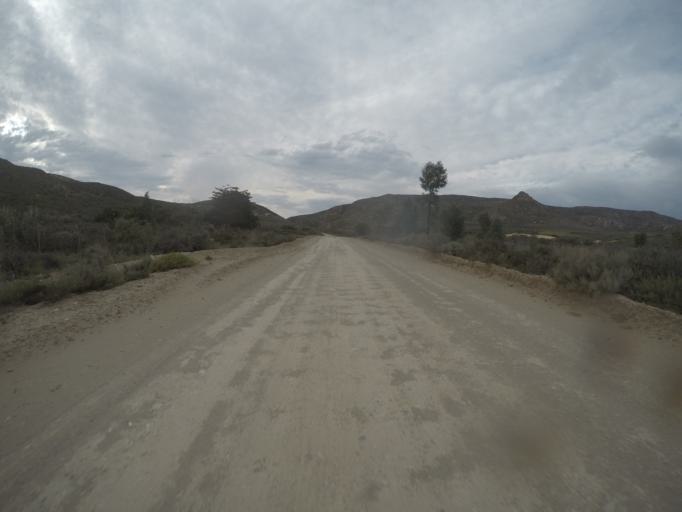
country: ZA
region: Eastern Cape
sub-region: Cacadu District Municipality
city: Willowmore
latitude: -33.4992
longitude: 23.6371
